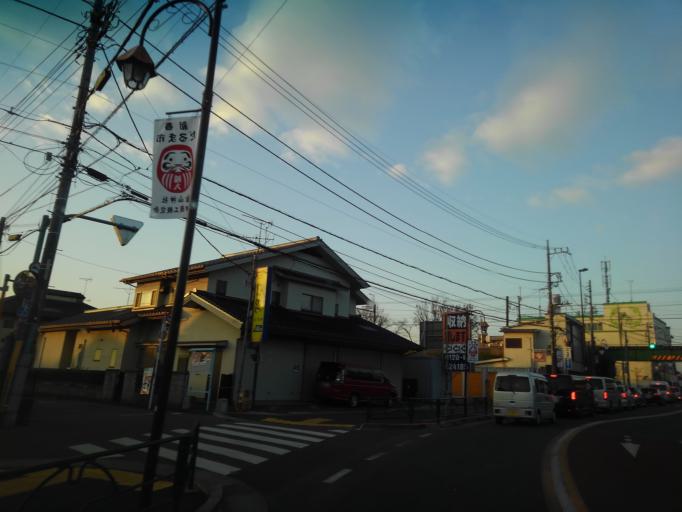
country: JP
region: Tokyo
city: Higashimurayama-shi
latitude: 35.7561
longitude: 139.4451
